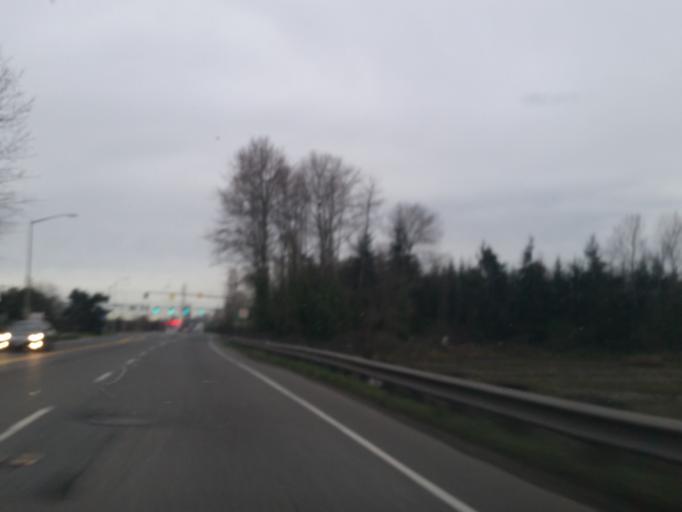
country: US
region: Washington
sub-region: King County
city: White Center
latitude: 47.5356
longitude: -122.3371
